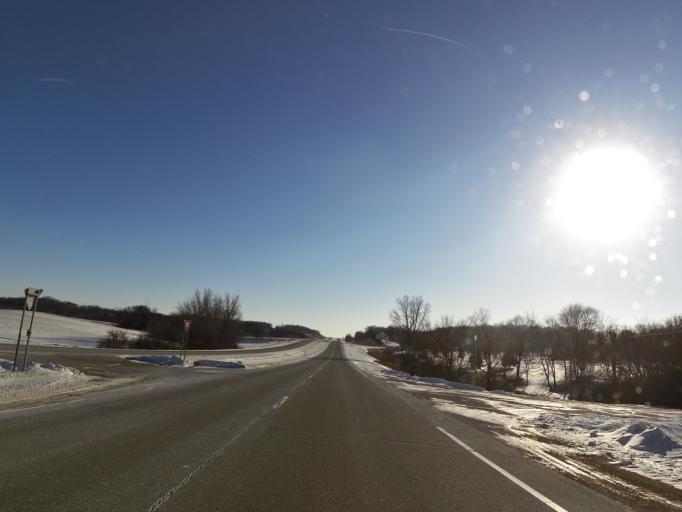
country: US
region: Minnesota
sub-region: Le Sueur County
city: New Prague
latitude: 44.5615
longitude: -93.5018
